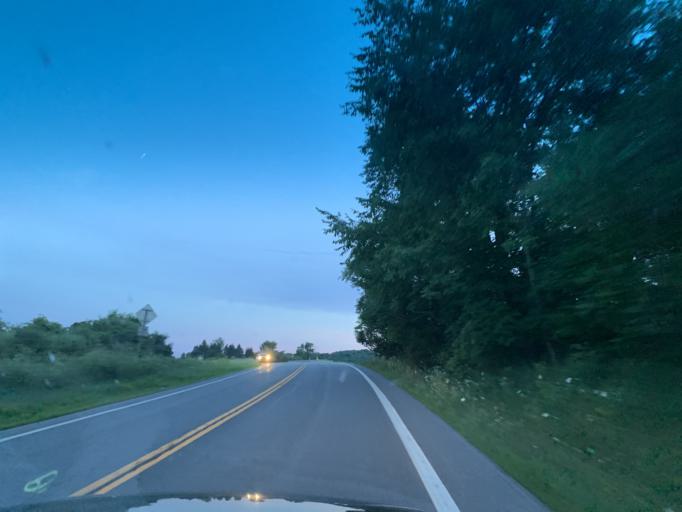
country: US
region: New York
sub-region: Chenango County
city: New Berlin
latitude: 42.6531
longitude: -75.3318
